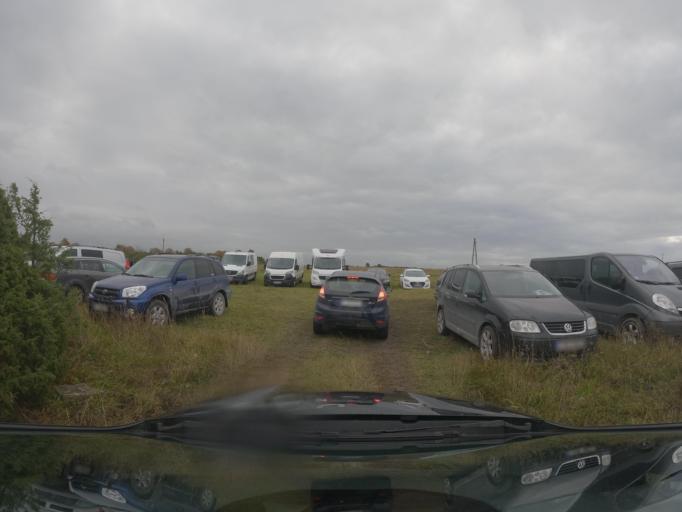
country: EE
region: Saare
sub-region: Kuressaare linn
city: Kuressaare
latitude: 58.4460
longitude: 21.9692
